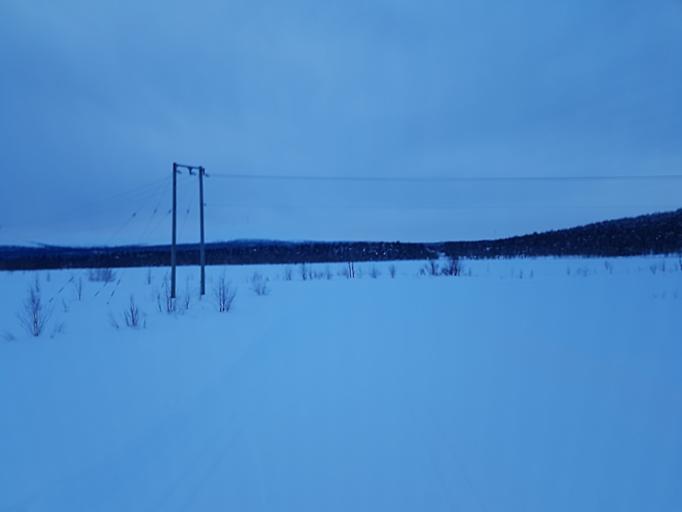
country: FI
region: Lapland
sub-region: Tunturi-Lappi
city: Kolari
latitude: 67.6172
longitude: 24.1319
